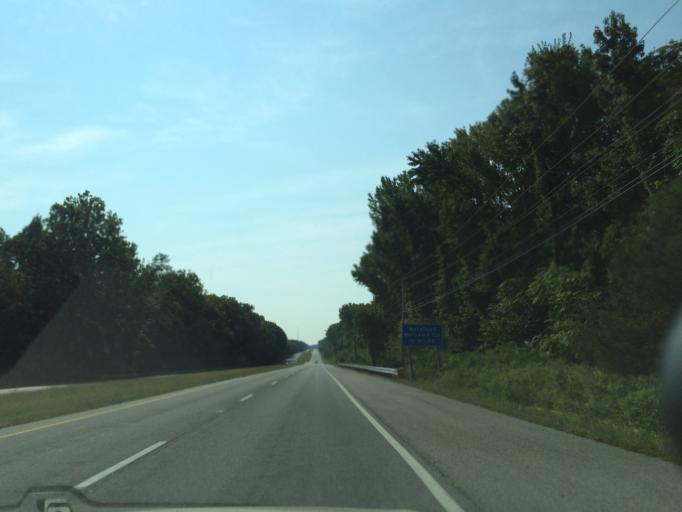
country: US
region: Maryland
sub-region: Charles County
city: La Plata
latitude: 38.4354
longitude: -76.9768
